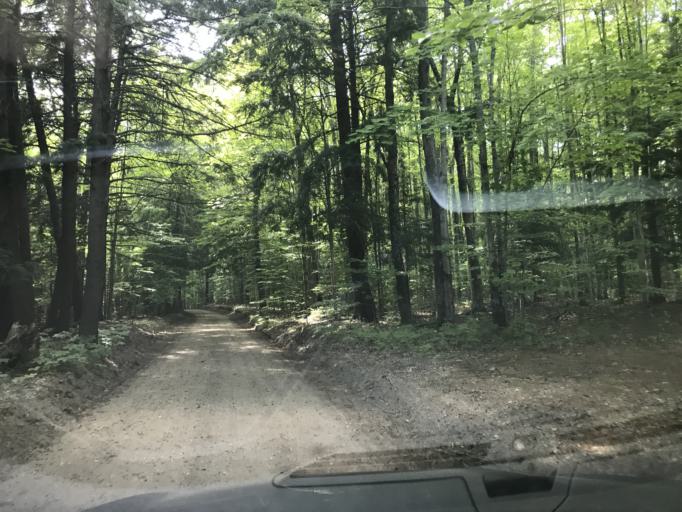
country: US
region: Michigan
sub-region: Cheboygan County
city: Indian River
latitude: 45.5928
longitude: -84.6803
